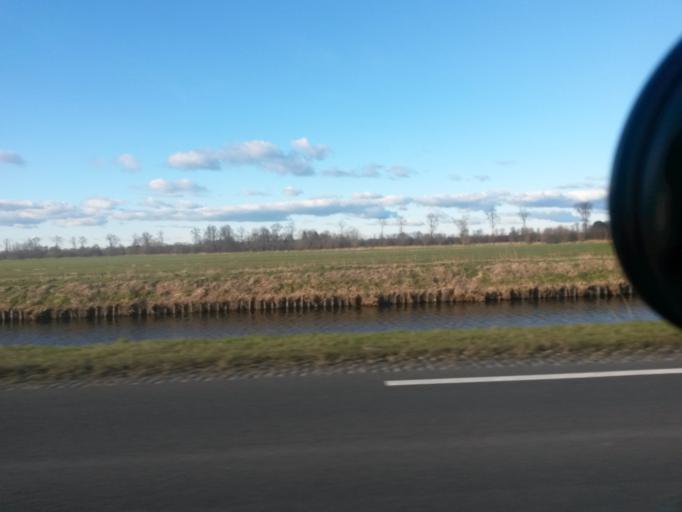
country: NL
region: Drenthe
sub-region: Gemeente Coevorden
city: Coevorden
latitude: 52.6551
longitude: 6.6703
